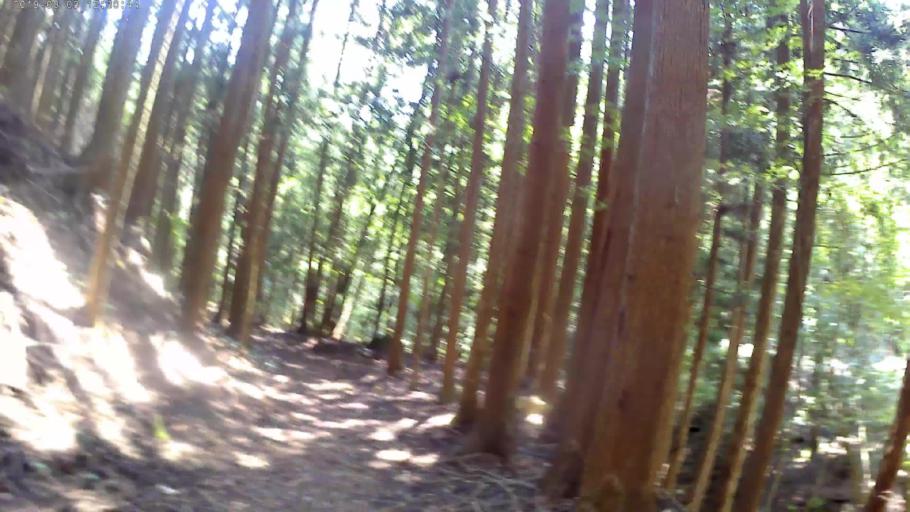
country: JP
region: Yamanashi
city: Enzan
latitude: 35.6093
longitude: 138.7904
